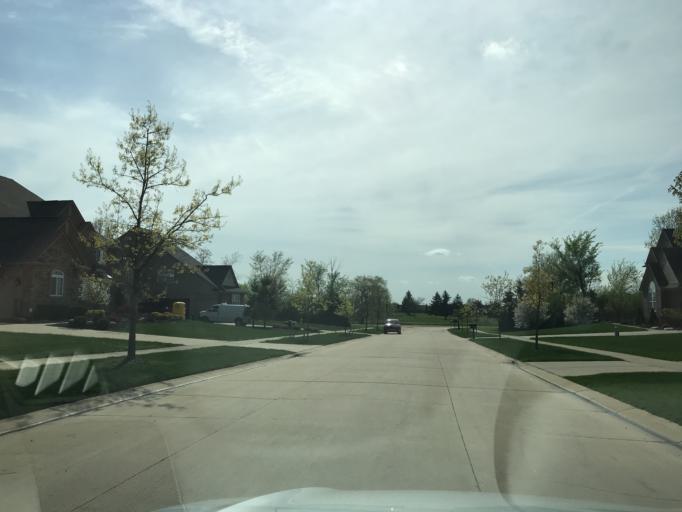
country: US
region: Michigan
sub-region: Oakland County
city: Wixom
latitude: 42.4606
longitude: -83.5714
